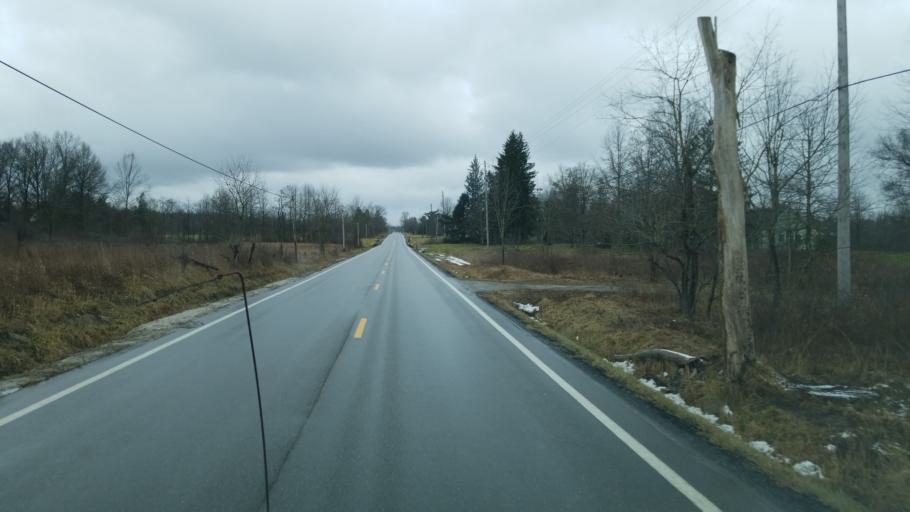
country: US
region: Ohio
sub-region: Trumbull County
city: Champion Heights
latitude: 41.3564
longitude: -80.9545
